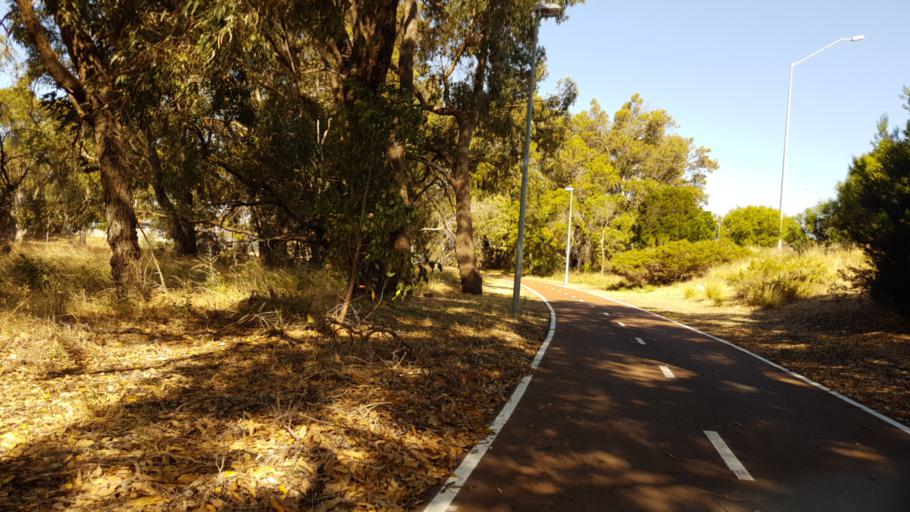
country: AU
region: Western Australia
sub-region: Stirling
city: Stirling
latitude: -31.8559
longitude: 115.8063
